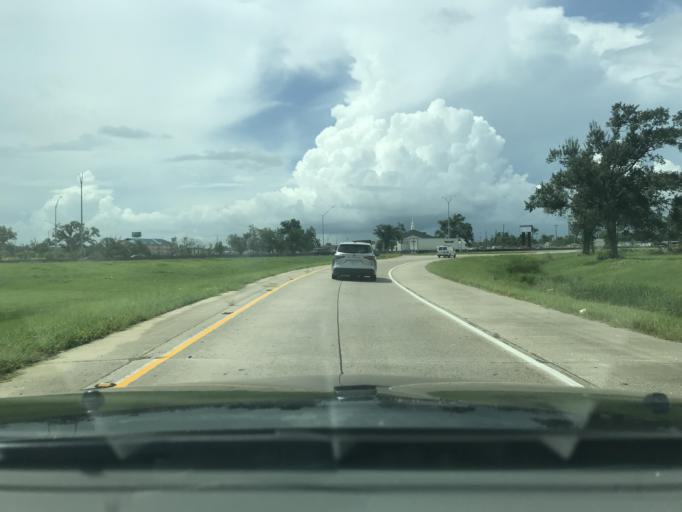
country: US
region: Louisiana
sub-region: Calcasieu Parish
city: Lake Charles
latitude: 30.2468
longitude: -93.1821
